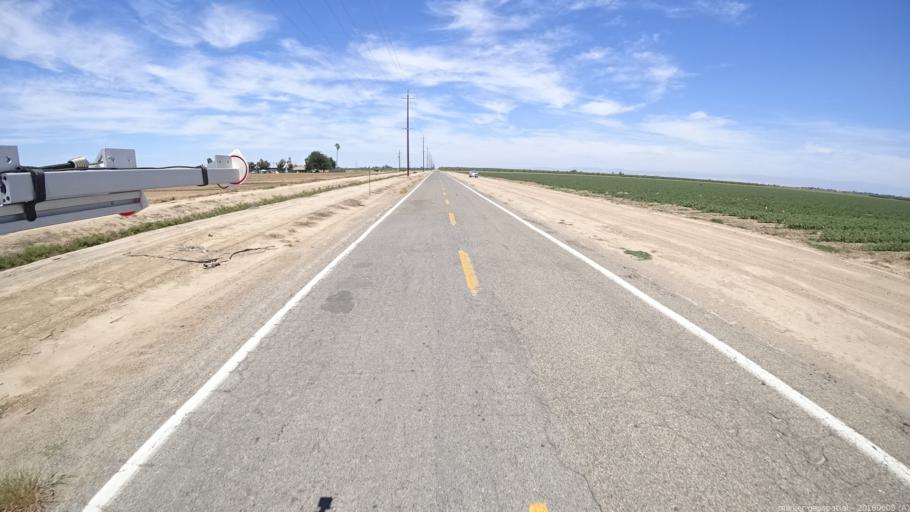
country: US
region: California
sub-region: Madera County
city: Chowchilla
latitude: 37.1025
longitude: -120.3109
